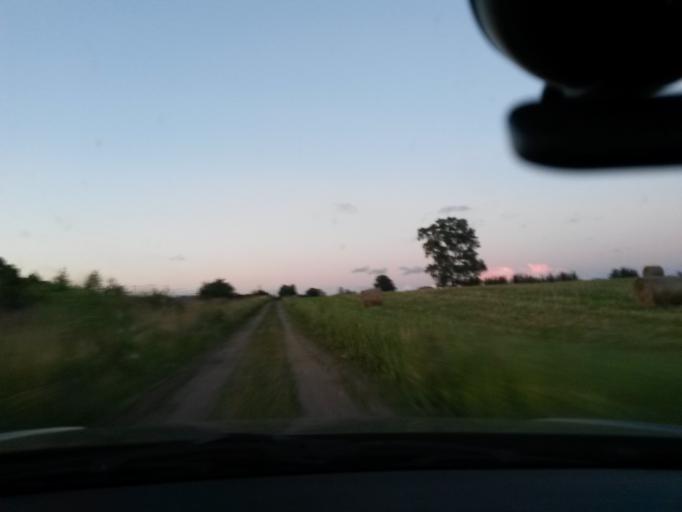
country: LV
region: Cesvaine
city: Cesvaine
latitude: 56.9495
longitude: 26.4006
